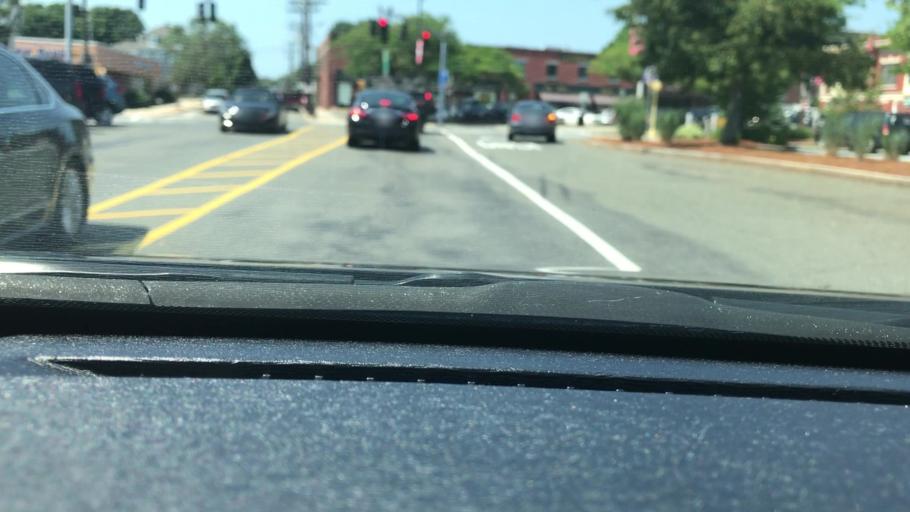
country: US
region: Massachusetts
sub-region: Middlesex County
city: Wakefield
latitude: 42.5025
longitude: -71.0691
